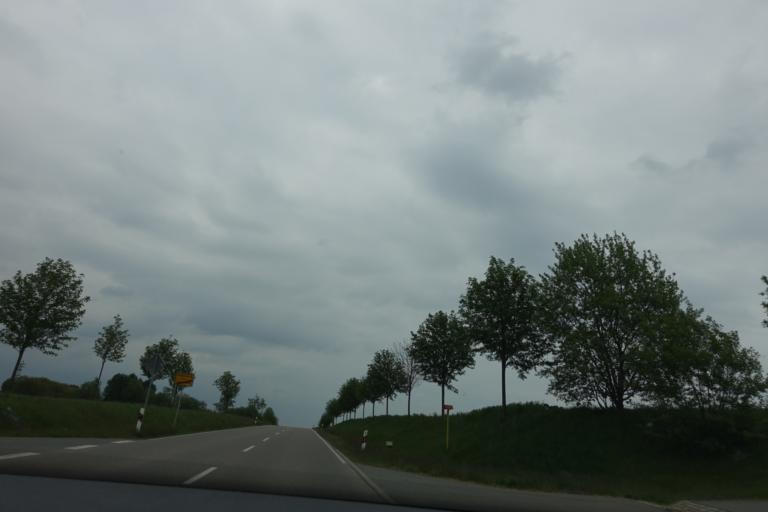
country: DE
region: Saxony
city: Augustusburg
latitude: 50.8100
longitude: 13.1091
